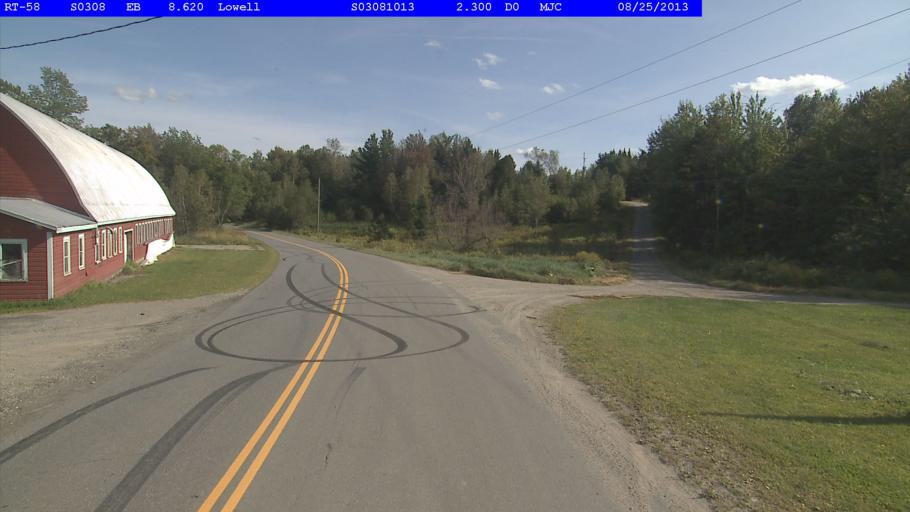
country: US
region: Vermont
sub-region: Lamoille County
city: Hyde Park
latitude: 44.8161
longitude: -72.4720
